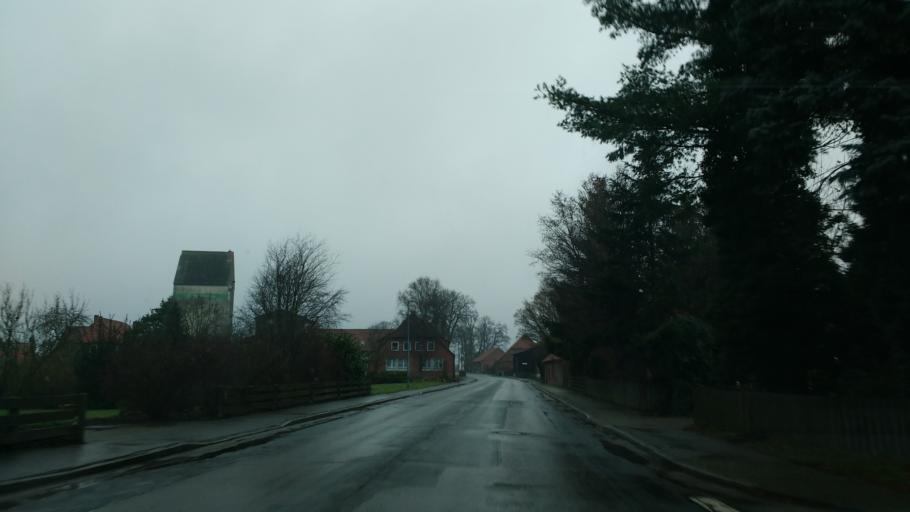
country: DE
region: Lower Saxony
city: Schwarmstedt
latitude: 52.6455
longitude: 9.5733
